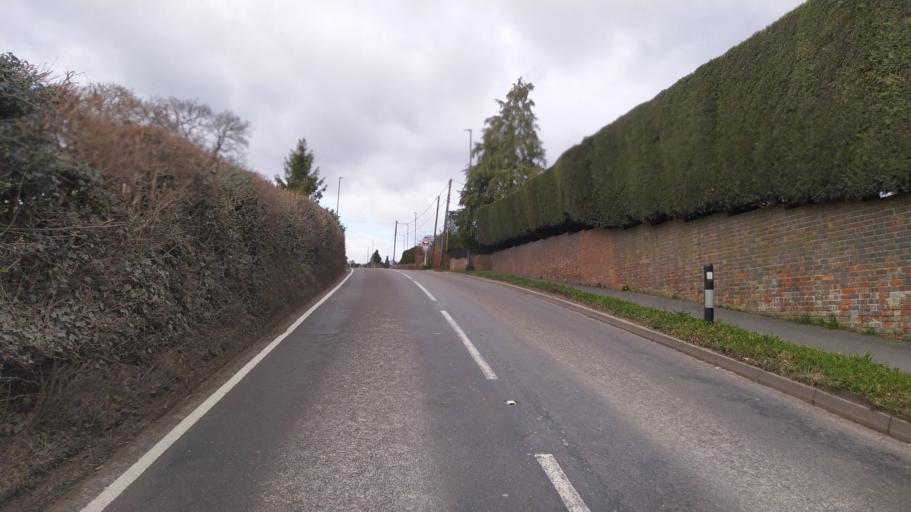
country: GB
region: England
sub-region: Surrey
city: Farnham
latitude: 51.2285
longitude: -0.8064
